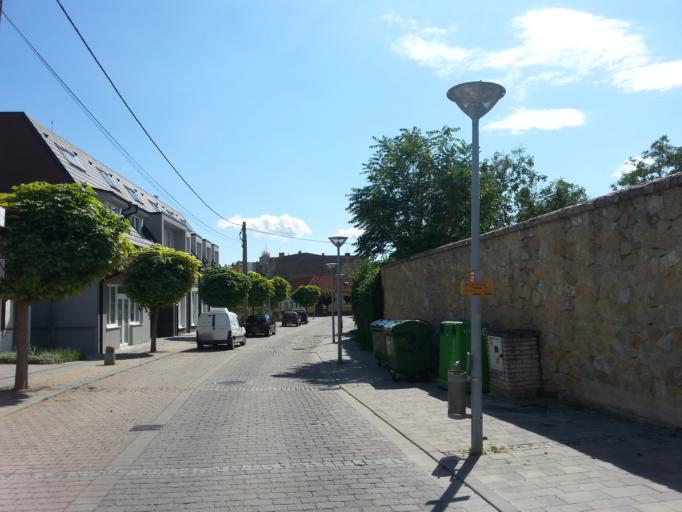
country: SK
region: Trenciansky
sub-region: Okres Nove Mesto nad Vahom
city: Nove Mesto nad Vahom
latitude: 48.7592
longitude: 17.8326
